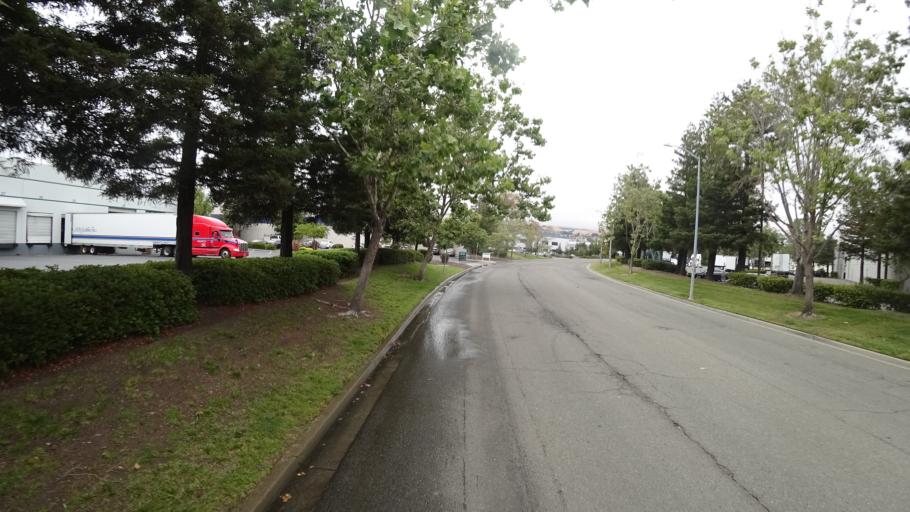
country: US
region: California
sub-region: Alameda County
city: Union City
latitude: 37.6164
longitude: -122.0607
